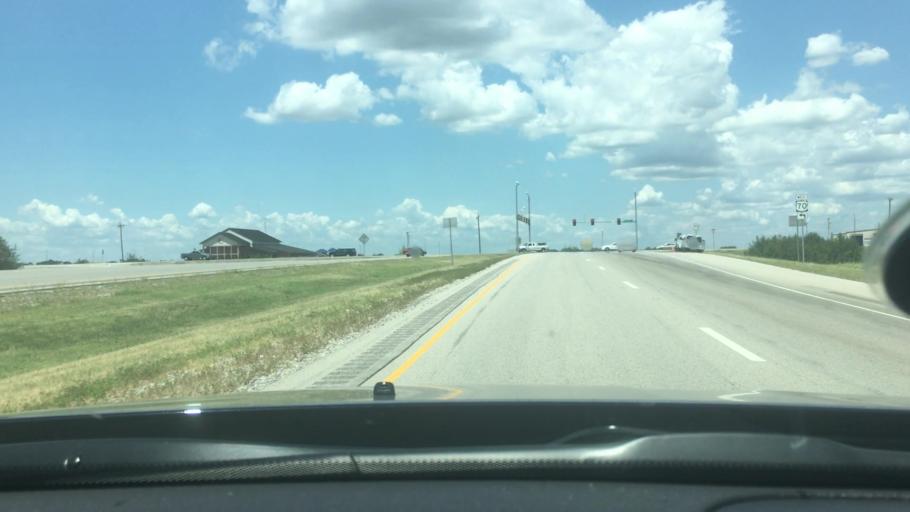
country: US
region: Oklahoma
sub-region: Bryan County
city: Durant
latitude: 33.9961
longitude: -96.4289
